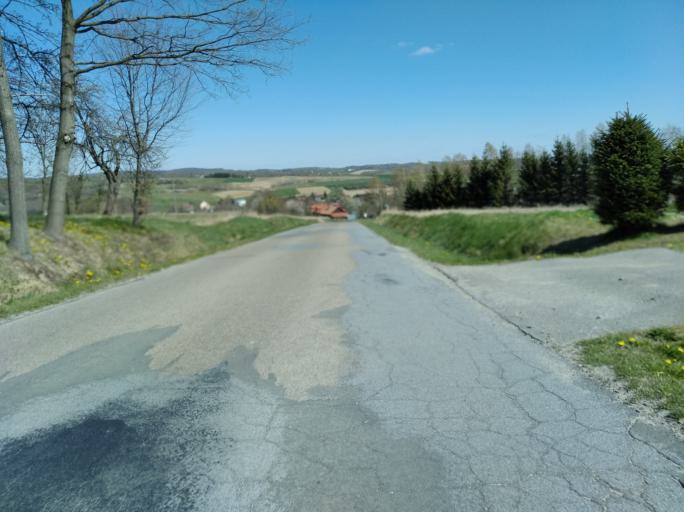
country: PL
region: Subcarpathian Voivodeship
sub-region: Powiat strzyzowski
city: Wisniowa
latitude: 49.9053
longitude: 21.6737
